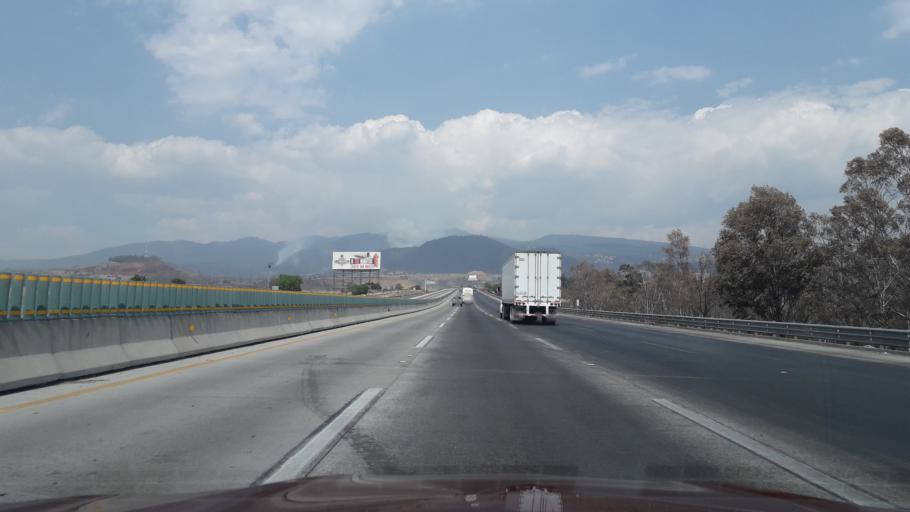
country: MX
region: Mexico
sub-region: Ixtapaluca
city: Jorge Jimenez Cantu
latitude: 19.3140
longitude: -98.8224
